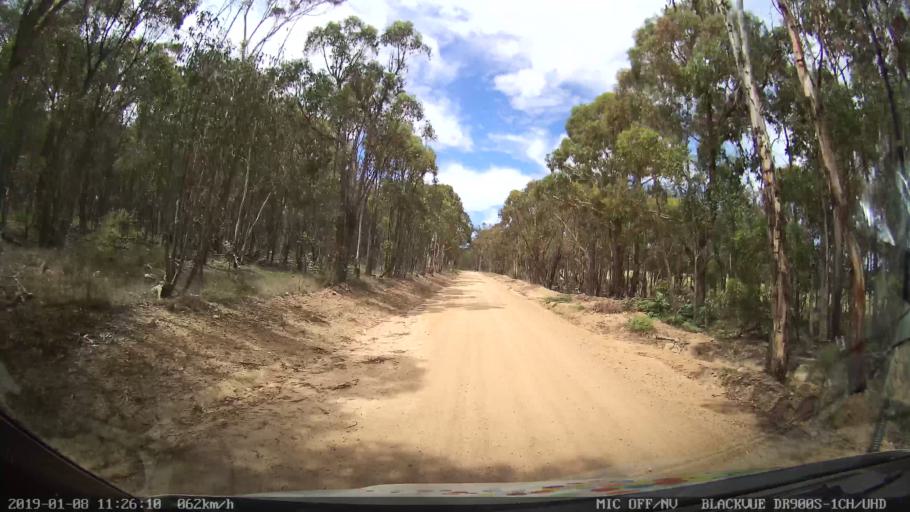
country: AU
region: New South Wales
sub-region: Guyra
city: Guyra
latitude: -30.2782
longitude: 151.5582
